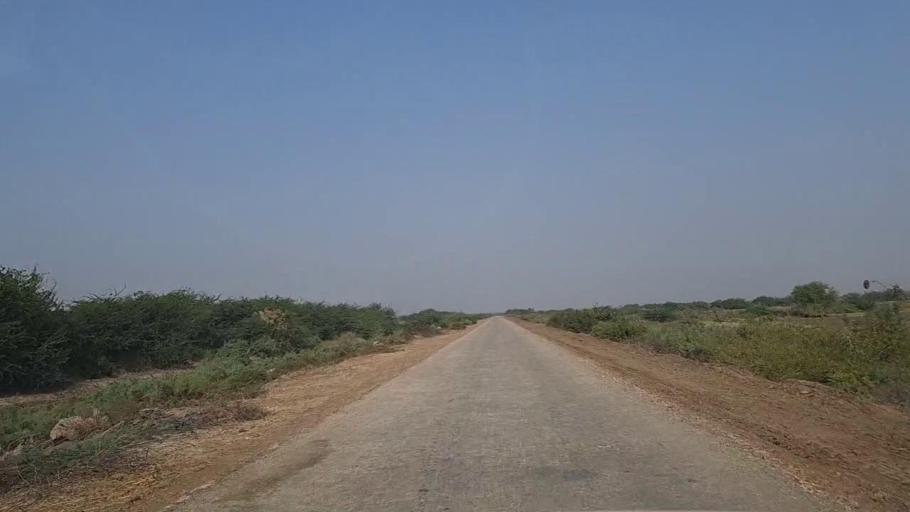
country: PK
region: Sindh
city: Keti Bandar
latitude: 24.2352
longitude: 67.6825
